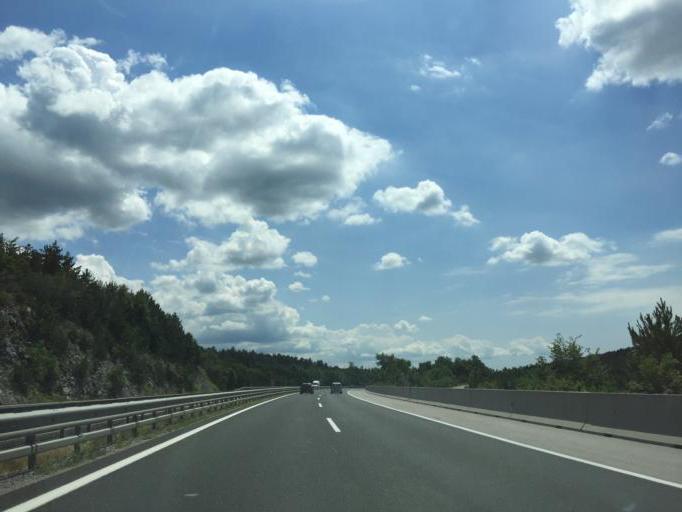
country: SI
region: Divaca
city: Divaca
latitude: 45.7102
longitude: 14.0020
